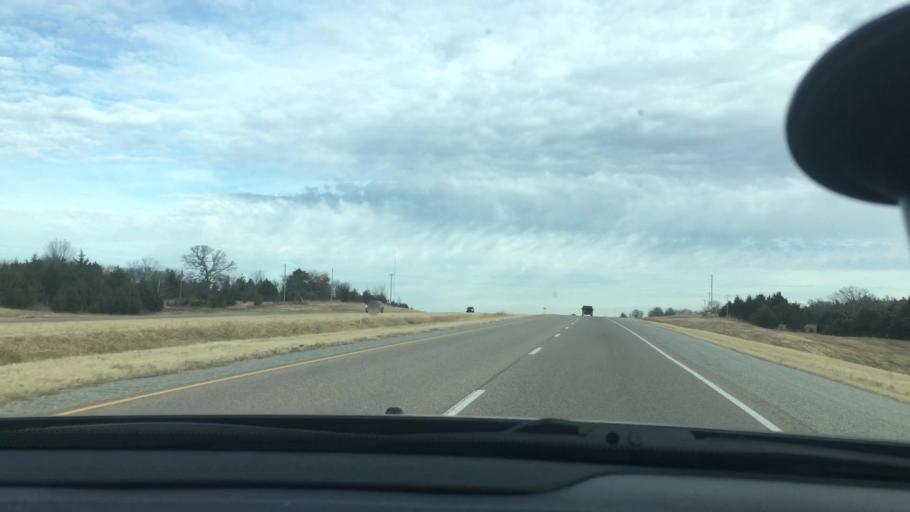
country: US
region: Oklahoma
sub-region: Pontotoc County
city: Byng
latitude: 34.8714
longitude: -96.6785
